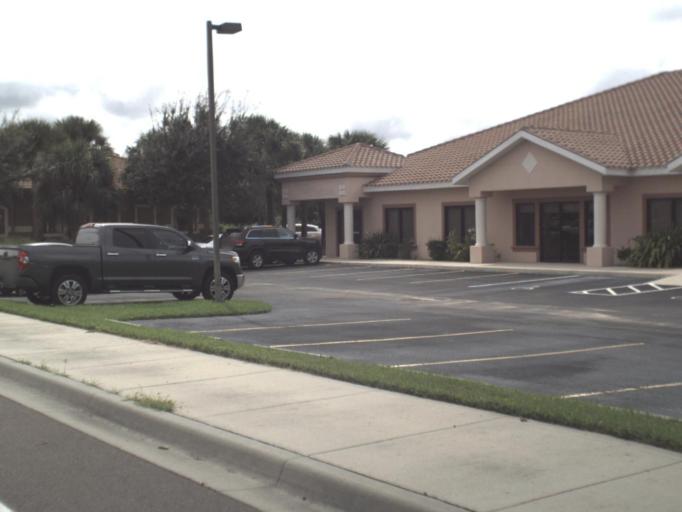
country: US
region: Florida
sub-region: Lee County
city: Villas
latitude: 26.5353
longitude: -81.8529
